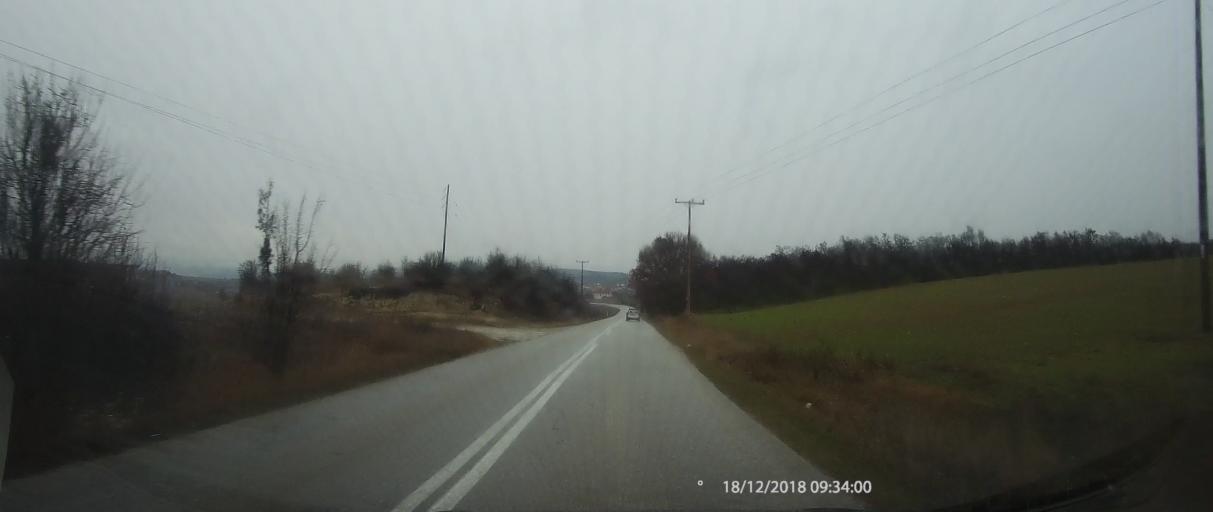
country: GR
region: Thessaly
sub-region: Nomos Larisis
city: Elassona
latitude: 39.9677
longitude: 22.1795
